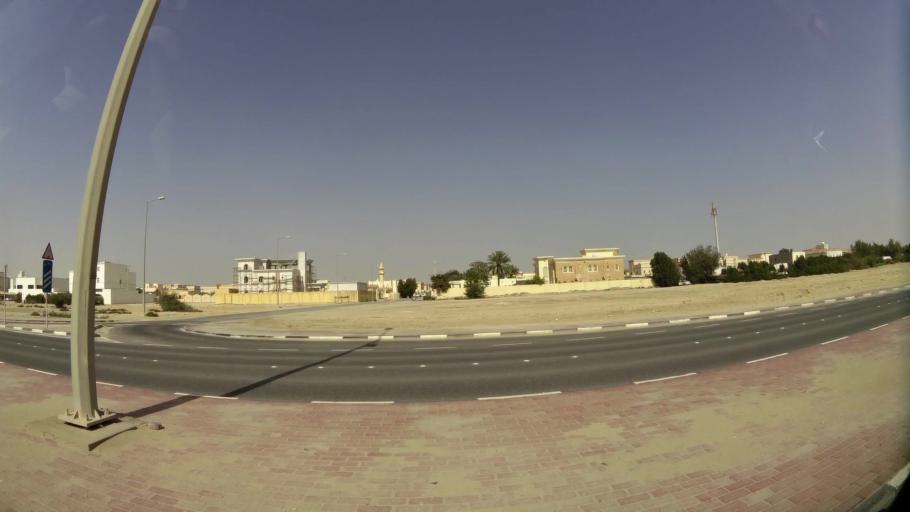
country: QA
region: Baladiyat Umm Salal
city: Umm Salal Muhammad
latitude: 25.3725
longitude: 51.4334
